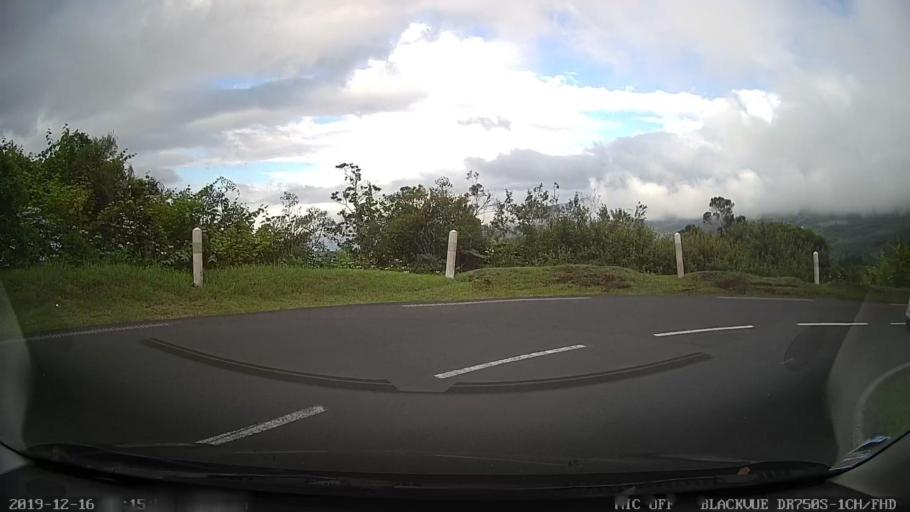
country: RE
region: Reunion
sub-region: Reunion
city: Cilaos
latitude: -21.1564
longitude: 55.5995
